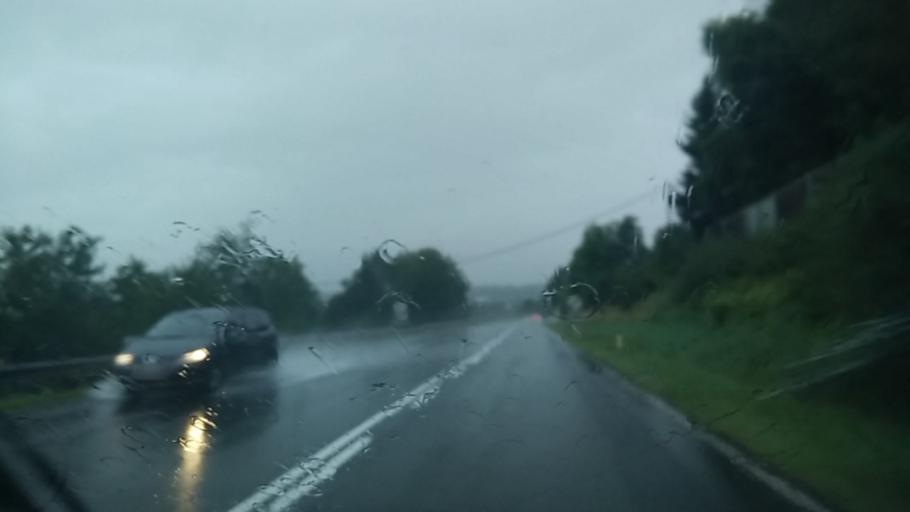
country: AT
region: Carinthia
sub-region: Politischer Bezirk Villach Land
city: Wernberg
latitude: 46.6250
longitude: 13.9239
